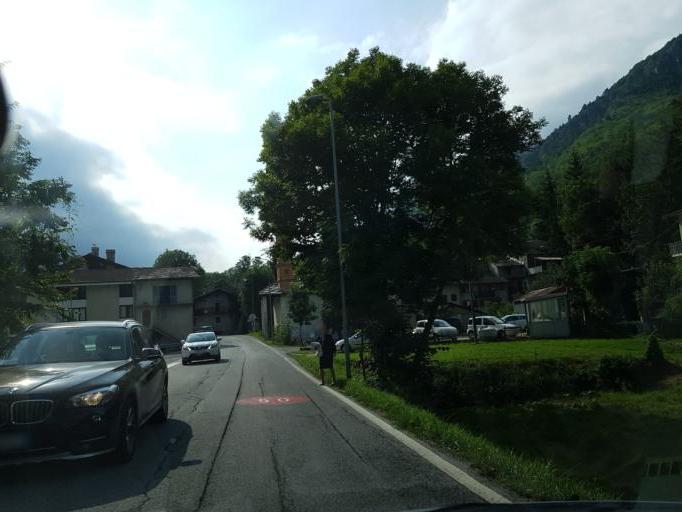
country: IT
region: Piedmont
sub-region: Provincia di Cuneo
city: Sampeyre
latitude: 44.5819
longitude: 7.1698
